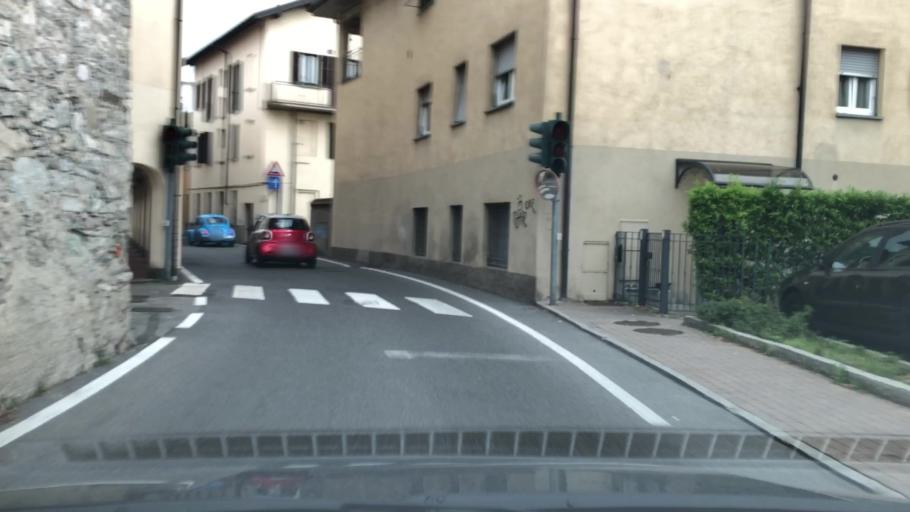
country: IT
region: Lombardy
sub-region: Provincia di Como
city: Casnate Con Bernate
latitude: 45.7574
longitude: 9.0737
